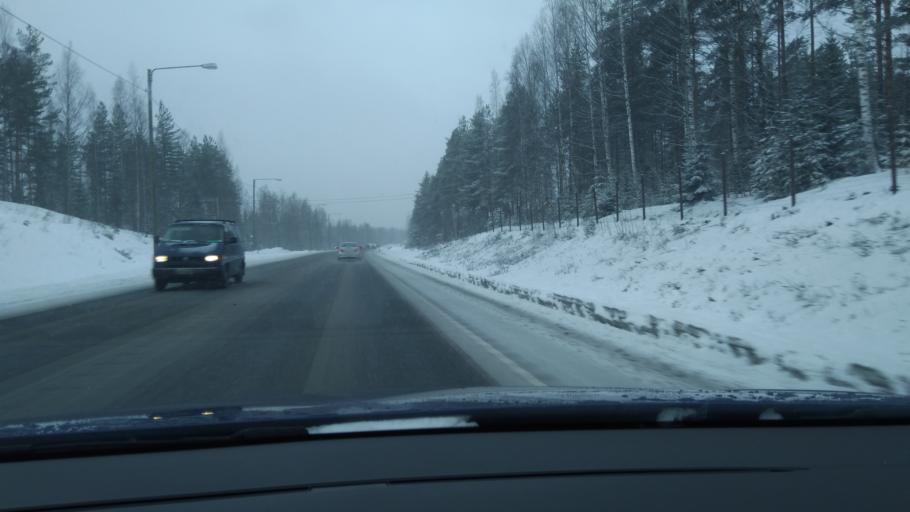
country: FI
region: Pirkanmaa
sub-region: Tampere
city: Kangasala
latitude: 61.5403
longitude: 24.0211
